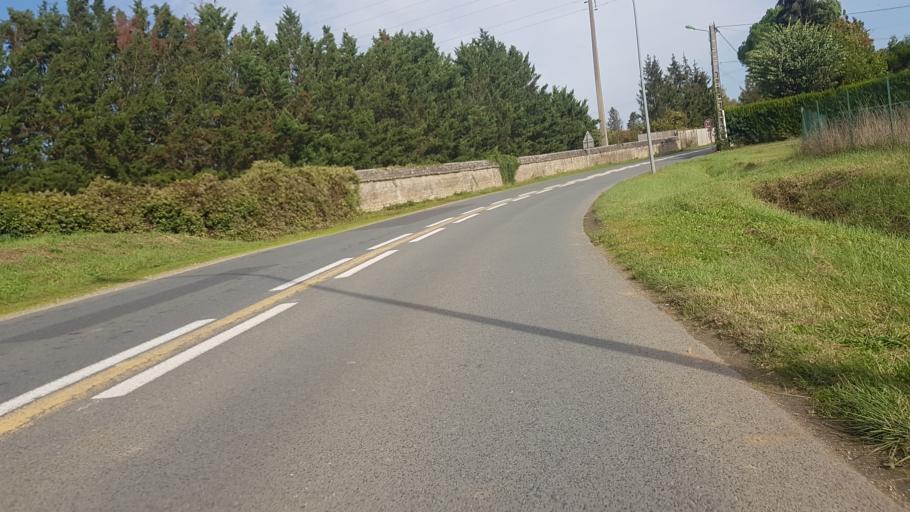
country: FR
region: Poitou-Charentes
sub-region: Departement de la Vienne
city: Chasseneuil-du-Poitou
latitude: 46.6278
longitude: 0.3664
